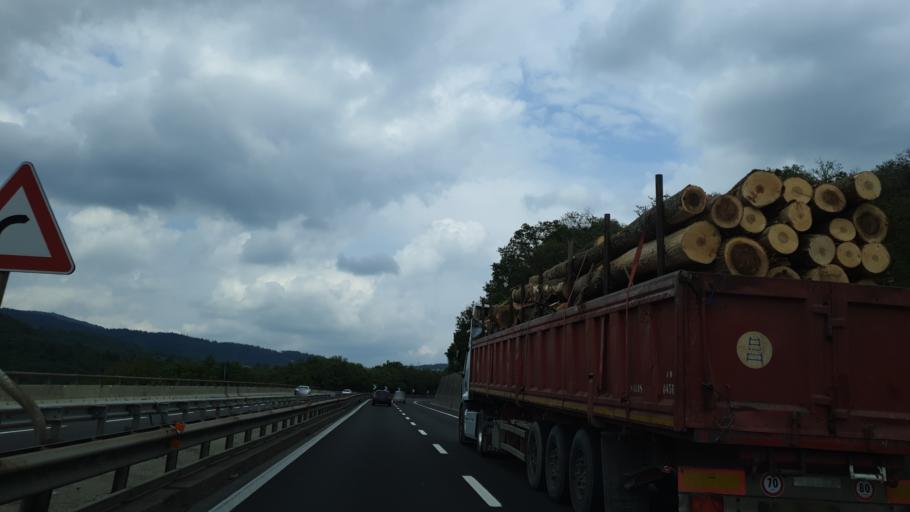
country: IT
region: Tuscany
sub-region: Province of Florence
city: Carraia
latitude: 43.9151
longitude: 11.1990
